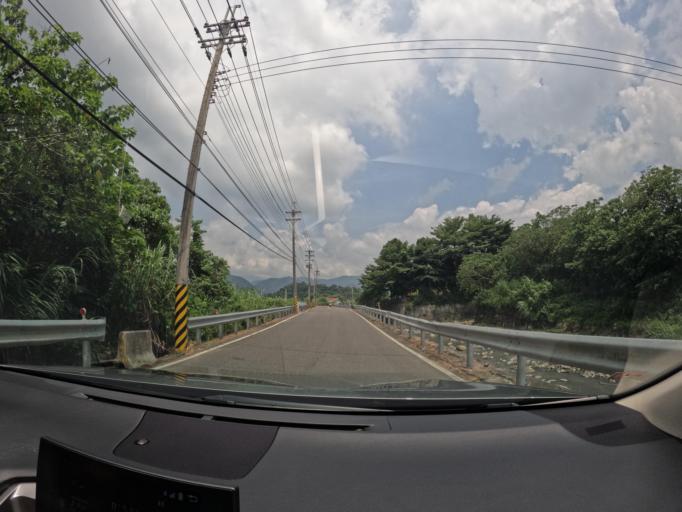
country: TW
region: Taiwan
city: Lugu
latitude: 23.8097
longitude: 120.8275
